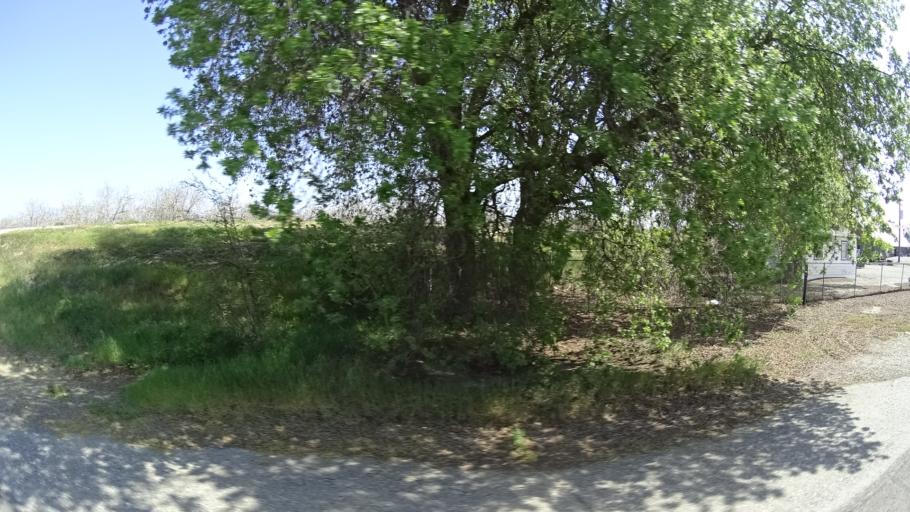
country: US
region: California
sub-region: Glenn County
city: Willows
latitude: 39.4883
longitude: -122.0206
